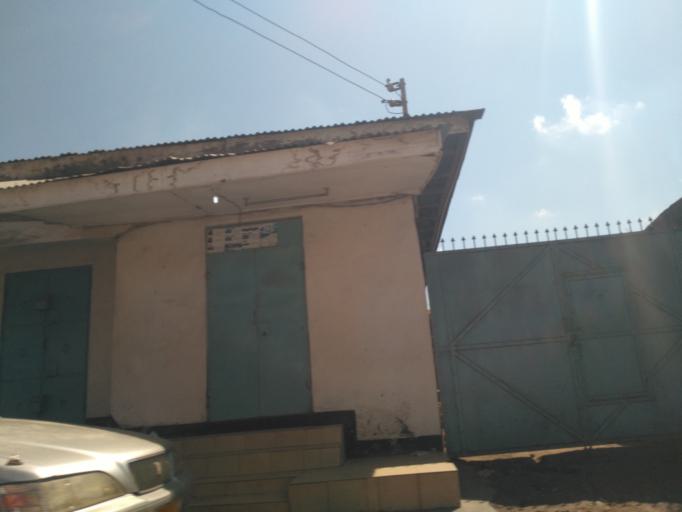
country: TZ
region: Arusha
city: Arusha
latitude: -3.3681
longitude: 36.6821
